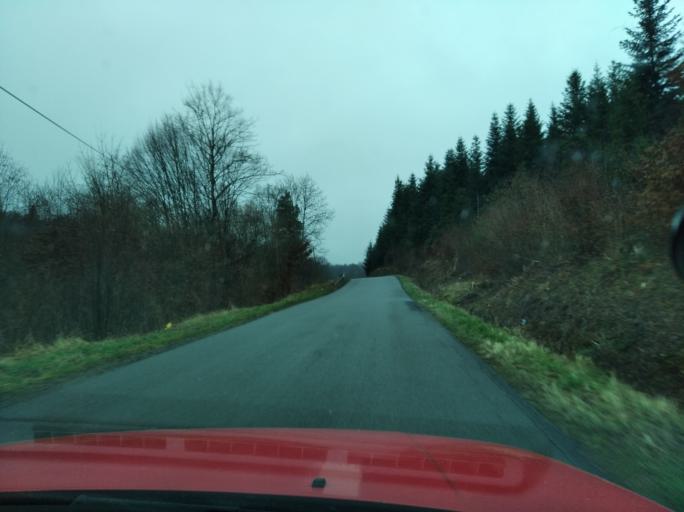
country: PL
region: Subcarpathian Voivodeship
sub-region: Powiat przemyski
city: Nienadowa
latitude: 49.8627
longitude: 22.4229
